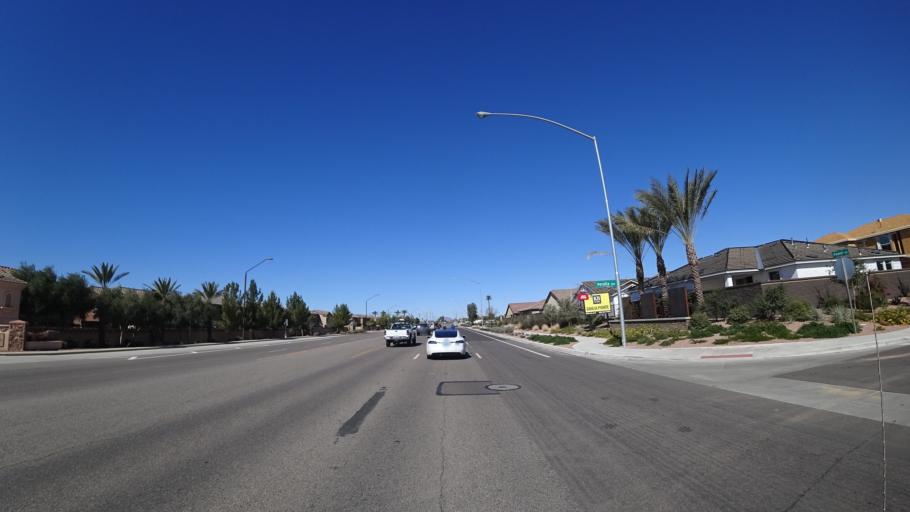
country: US
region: Arizona
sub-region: Maricopa County
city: Gilbert
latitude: 33.3587
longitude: -111.6875
